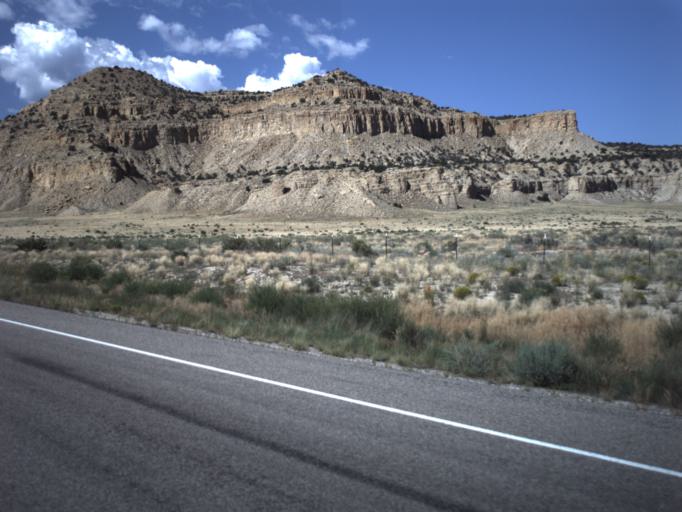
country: US
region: Utah
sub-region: Emery County
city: Ferron
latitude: 38.8466
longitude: -111.3109
